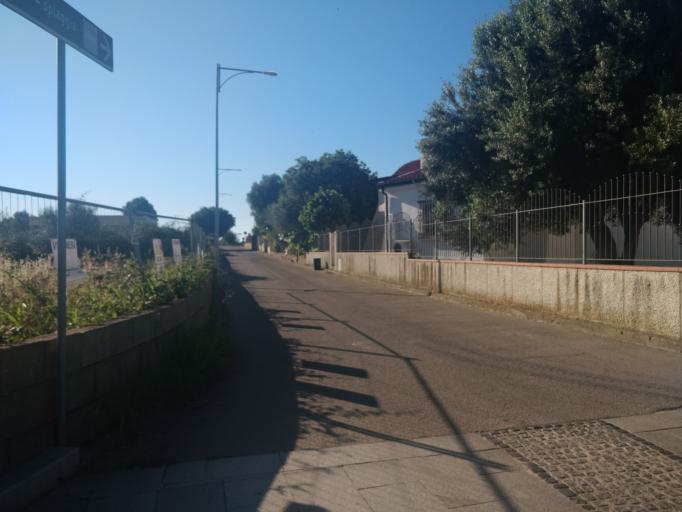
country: IT
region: Sardinia
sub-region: Provincia di Ogliastra
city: Girasole
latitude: 39.9531
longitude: 9.6639
